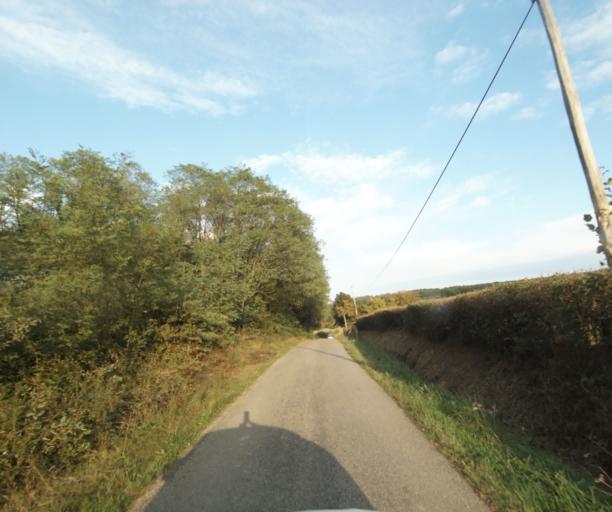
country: FR
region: Bourgogne
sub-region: Departement de Saone-et-Loire
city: Charolles
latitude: 46.4382
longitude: 4.3618
